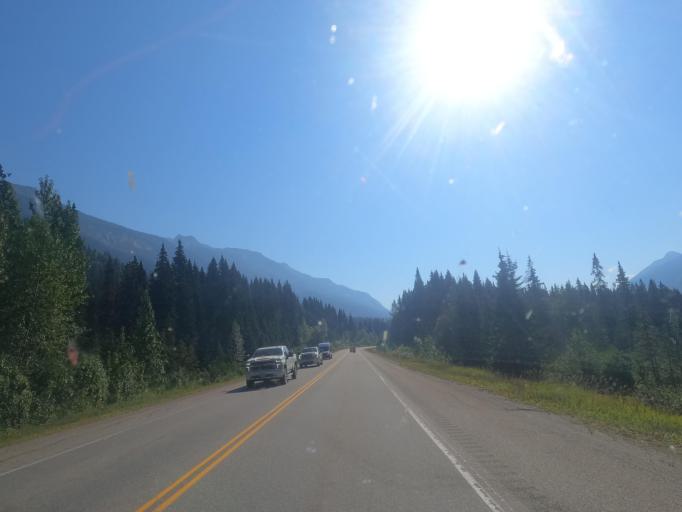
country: CA
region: Alberta
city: Grande Cache
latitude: 53.0018
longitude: -119.0378
